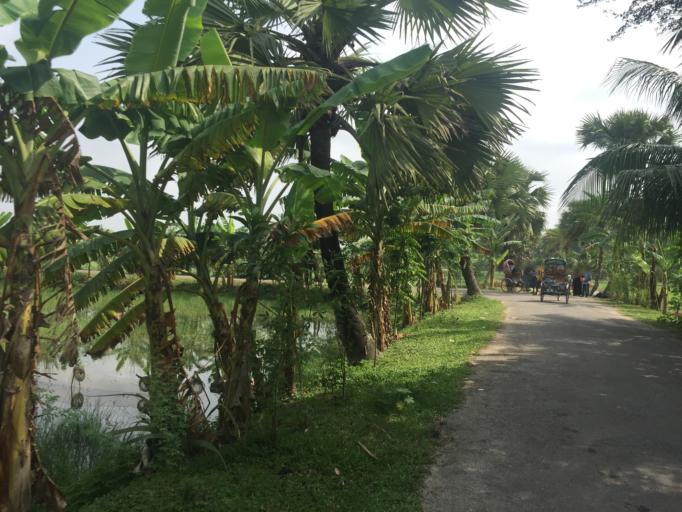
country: BD
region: Barisal
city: Mathba
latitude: 22.2520
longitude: 89.9162
